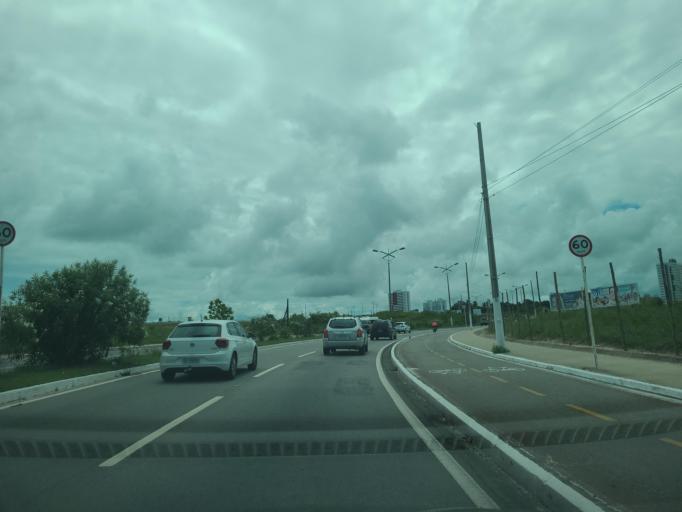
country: BR
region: Alagoas
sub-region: Maceio
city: Maceio
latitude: -9.6282
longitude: -35.7027
